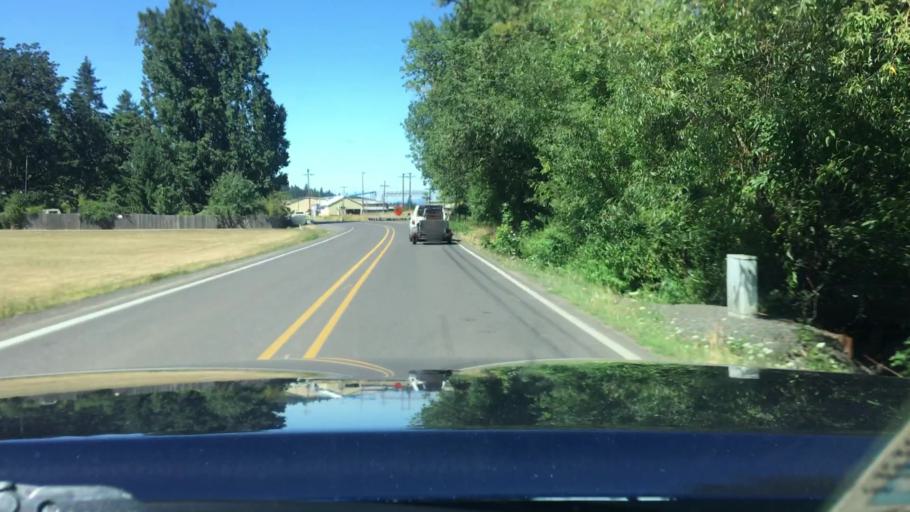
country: US
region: Oregon
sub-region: Lane County
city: Cottage Grove
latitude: 43.8305
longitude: -123.0451
